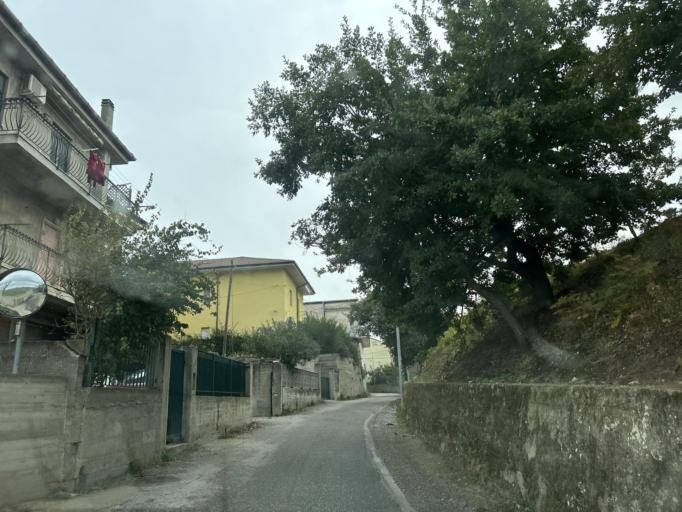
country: IT
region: Calabria
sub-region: Provincia di Catanzaro
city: Staletti
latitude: 38.7661
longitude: 16.5377
